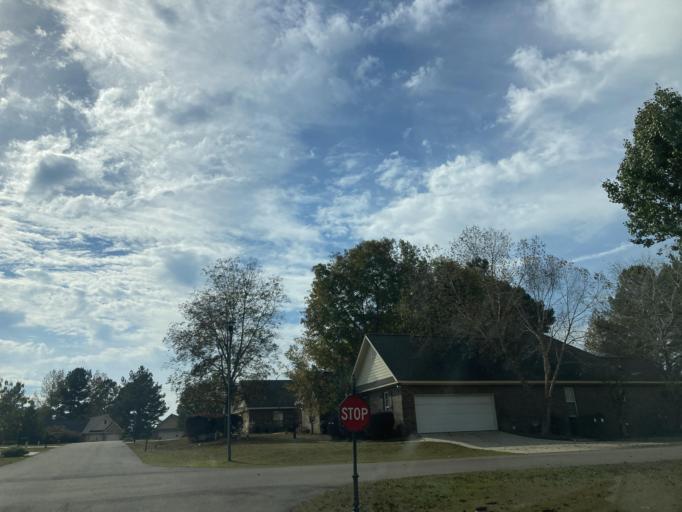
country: US
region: Mississippi
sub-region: Lamar County
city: West Hattiesburg
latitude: 31.3324
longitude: -89.4335
